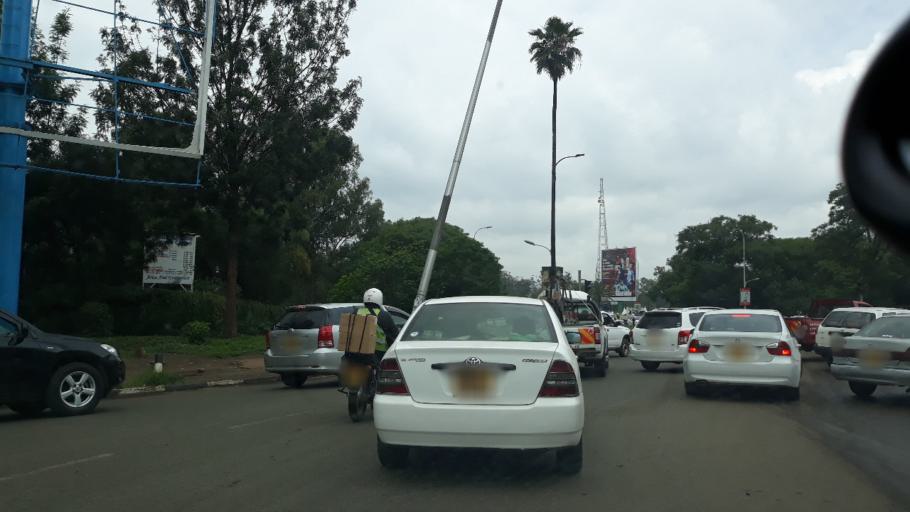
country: KE
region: Nairobi Area
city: Nairobi
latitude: -1.2818
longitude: 36.8148
